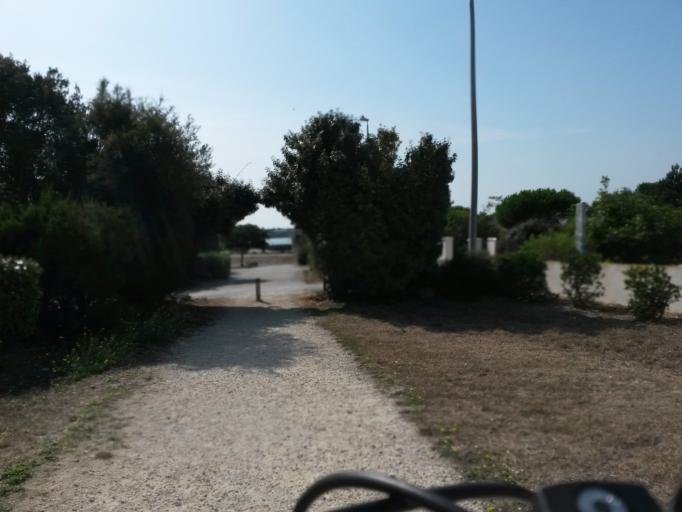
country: FR
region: Poitou-Charentes
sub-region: Departement de la Charente-Maritime
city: Nieul-sur-Mer
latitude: 46.2030
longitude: -1.2053
